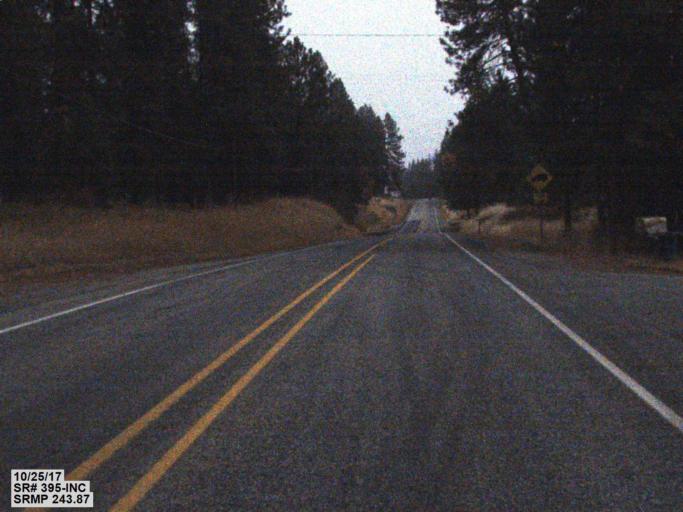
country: US
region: Washington
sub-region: Stevens County
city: Kettle Falls
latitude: 48.6541
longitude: -118.1139
